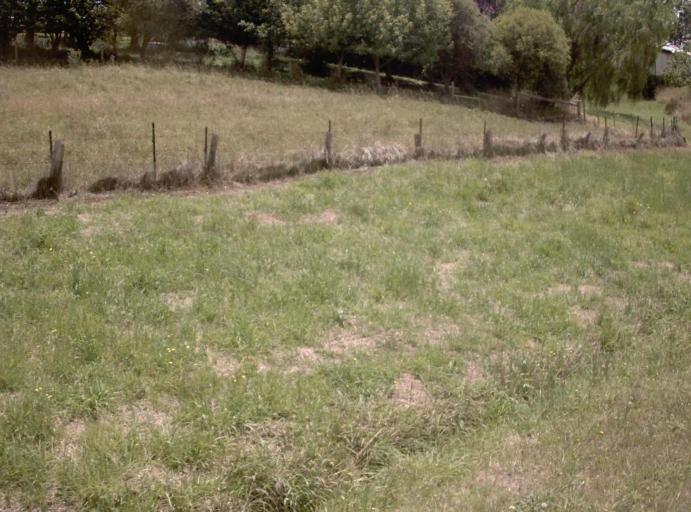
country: AU
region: Victoria
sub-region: Latrobe
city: Moe
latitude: -38.0140
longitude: 146.3710
